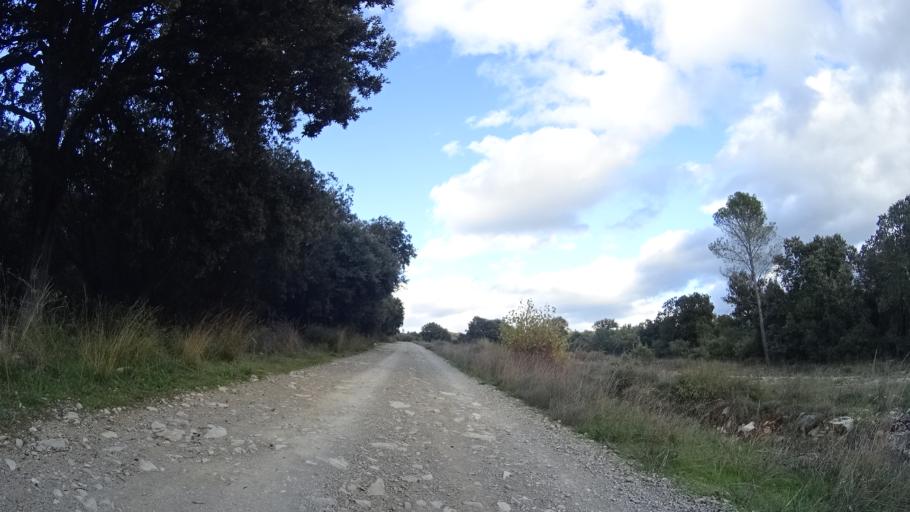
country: FR
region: Languedoc-Roussillon
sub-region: Departement de l'Herault
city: Claret
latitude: 43.8610
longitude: 3.9103
